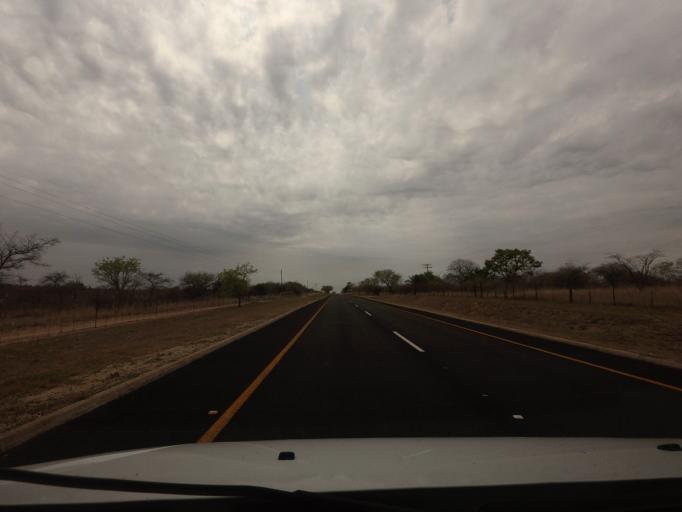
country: ZA
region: Limpopo
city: Thulamahashi
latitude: -24.5607
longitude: 31.1650
